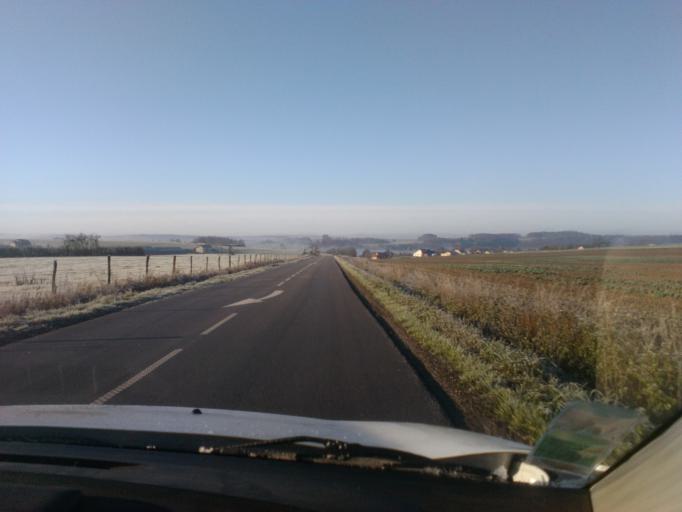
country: FR
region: Lorraine
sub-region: Departement des Vosges
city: Darnieulles
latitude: 48.1886
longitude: 6.2238
